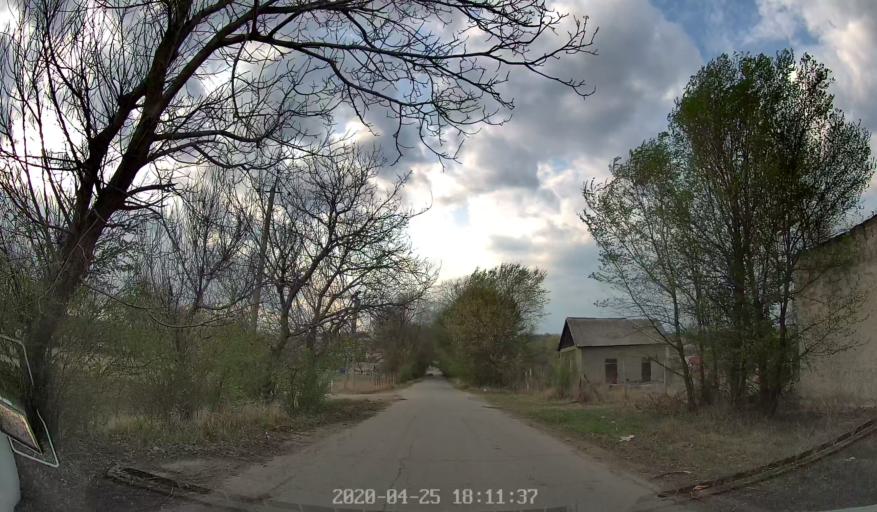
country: MD
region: Chisinau
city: Vadul lui Voda
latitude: 47.1398
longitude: 29.0697
